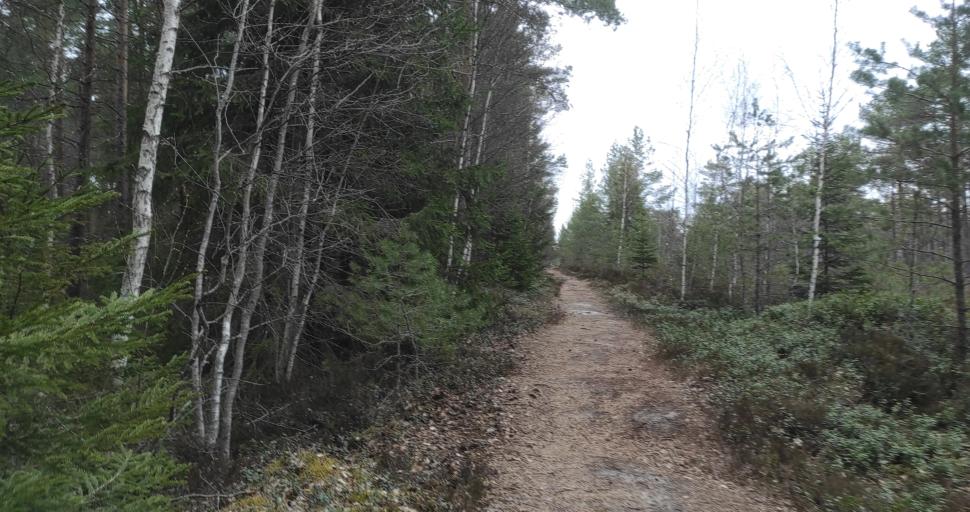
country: LV
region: Dundaga
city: Dundaga
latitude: 57.3461
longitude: 22.1497
